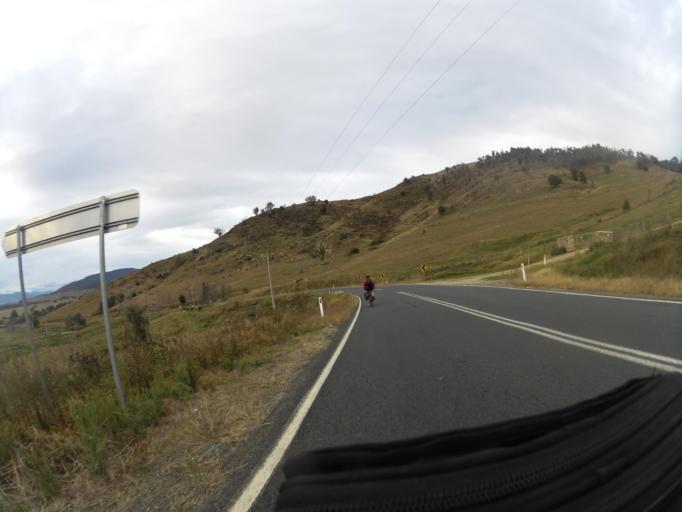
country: AU
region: New South Wales
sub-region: Snowy River
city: Jindabyne
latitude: -36.0859
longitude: 147.9774
